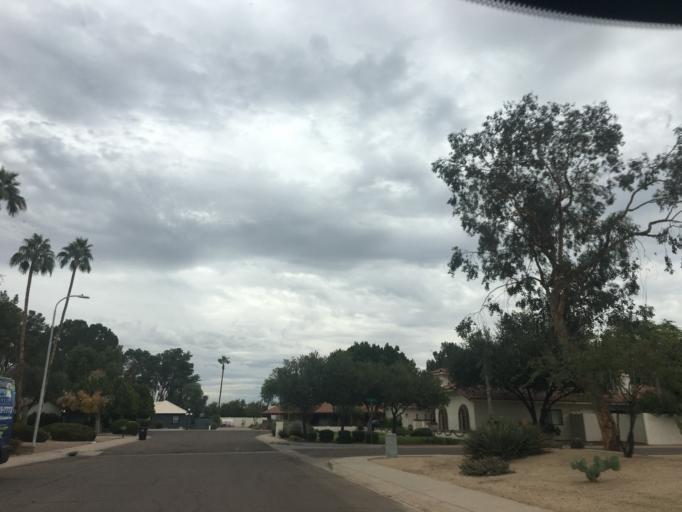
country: US
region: Arizona
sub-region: Maricopa County
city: Guadalupe
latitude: 33.3665
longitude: -111.9257
